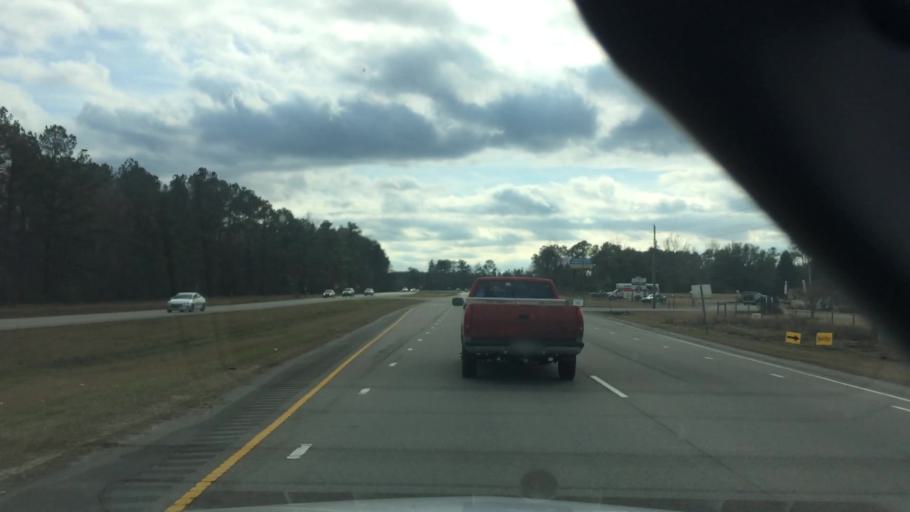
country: US
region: North Carolina
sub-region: Brunswick County
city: Bolivia
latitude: 34.1547
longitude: -78.0927
